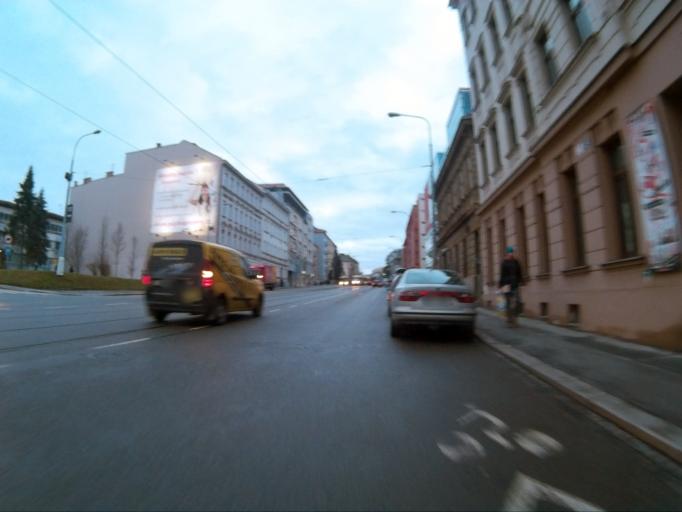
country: CZ
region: South Moravian
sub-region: Mesto Brno
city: Brno
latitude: 49.1851
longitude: 16.5951
